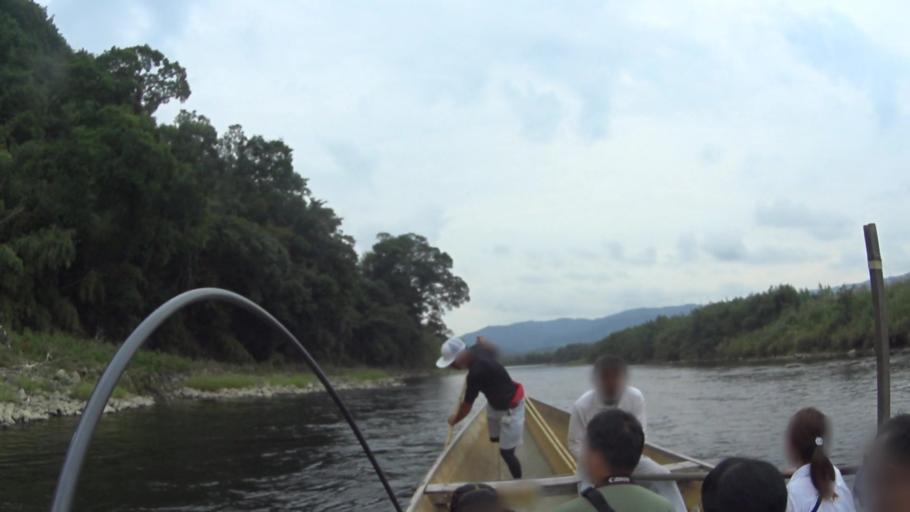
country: JP
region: Kyoto
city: Kameoka
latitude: 35.0183
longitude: 135.6000
